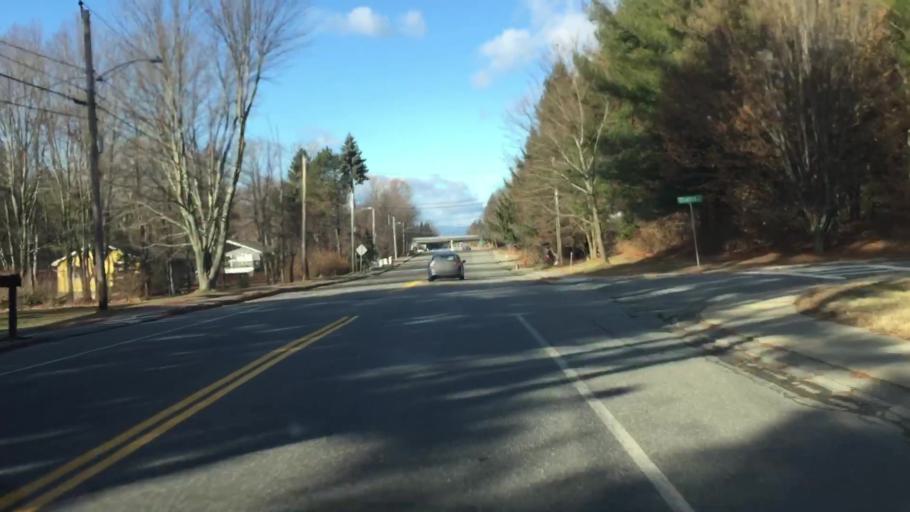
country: US
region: Massachusetts
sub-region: Worcester County
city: West Boylston
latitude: 42.3982
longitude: -71.7951
